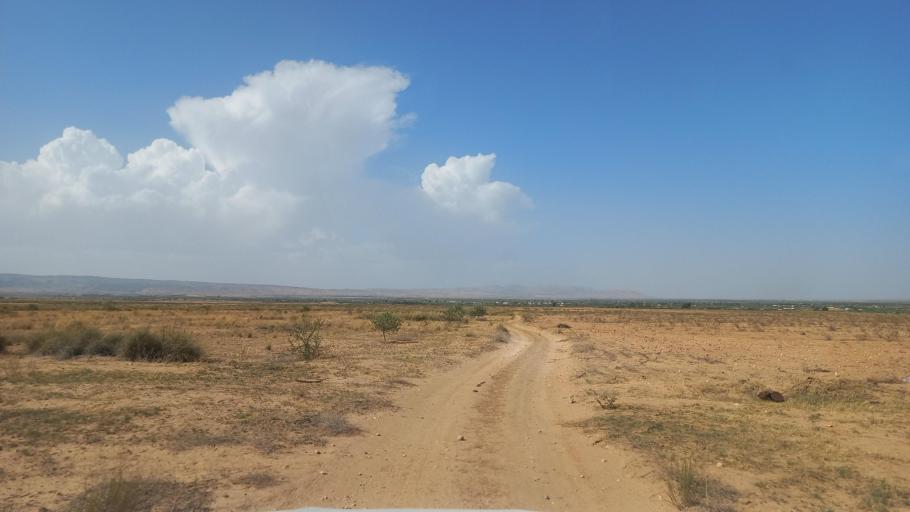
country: TN
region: Al Qasrayn
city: Kasserine
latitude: 35.2153
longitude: 9.0267
